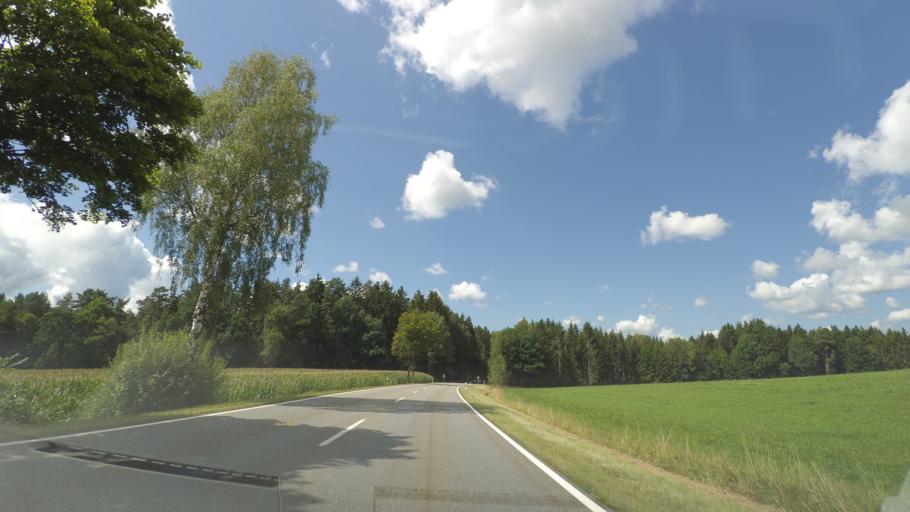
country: DE
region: Bavaria
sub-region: Lower Bavaria
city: Geiersthal
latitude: 49.0453
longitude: 12.9315
